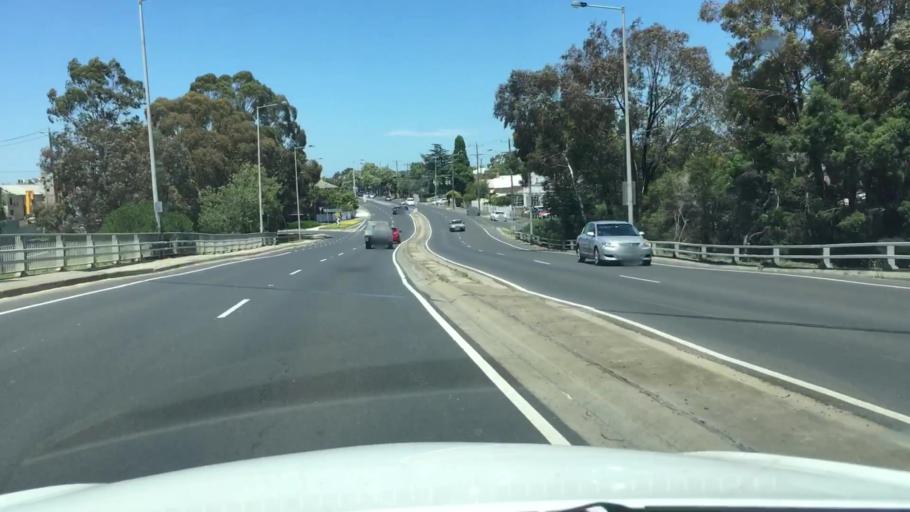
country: AU
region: Victoria
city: Spotswood
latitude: -37.8359
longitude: 144.8825
